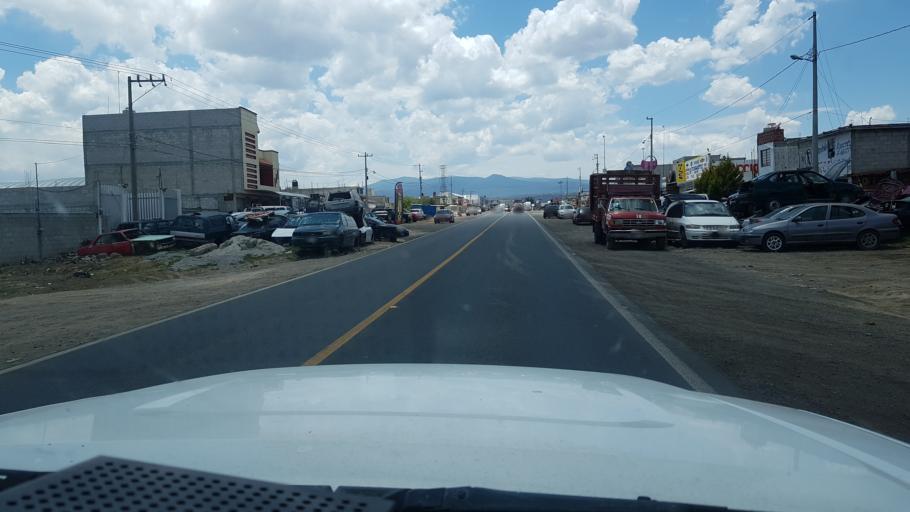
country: MX
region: Hidalgo
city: Calpulalpan
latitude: 19.6001
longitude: -98.5685
